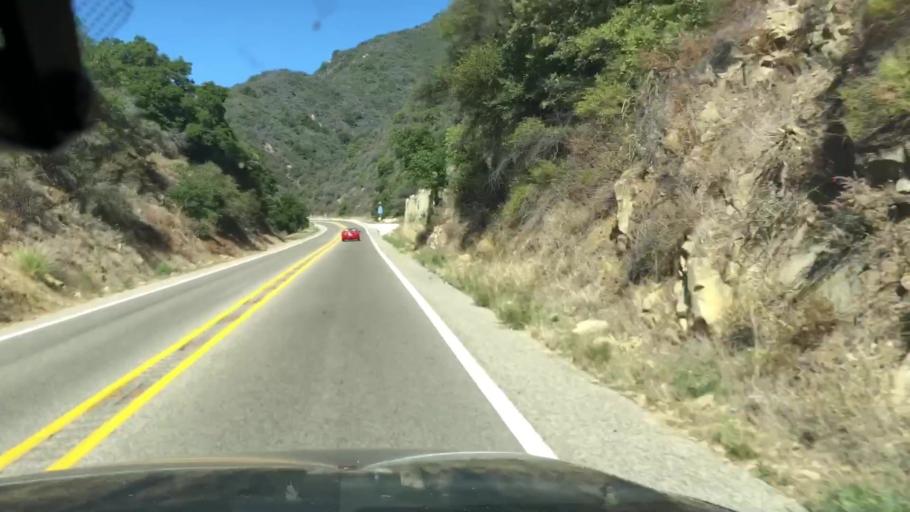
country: US
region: California
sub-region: Santa Barbara County
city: Goleta
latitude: 34.4988
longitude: -119.8009
